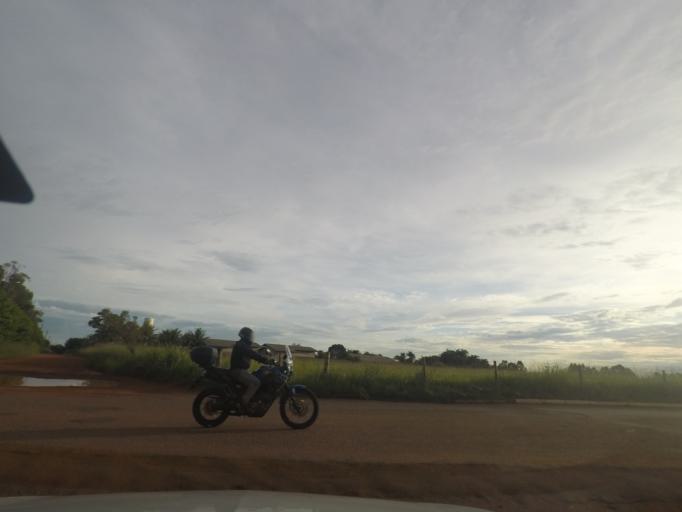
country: BR
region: Goias
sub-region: Trindade
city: Trindade
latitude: -16.7192
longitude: -49.4400
